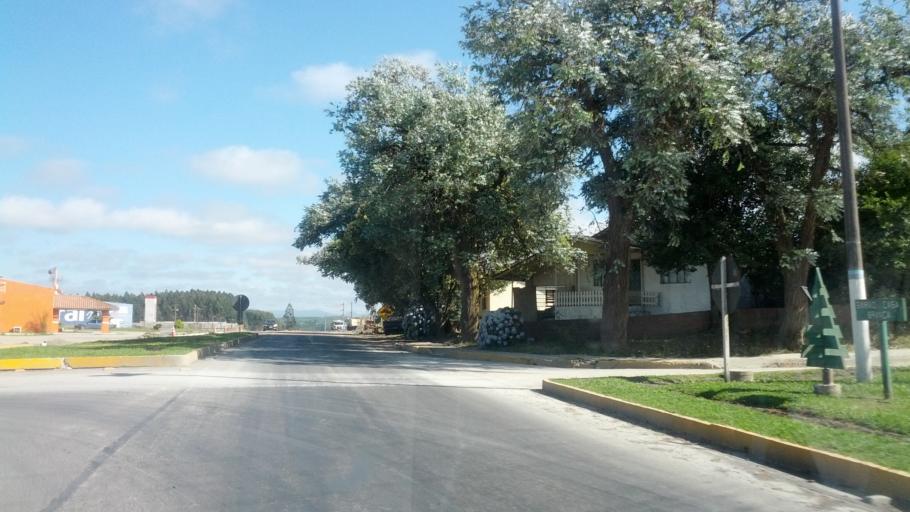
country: BR
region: Santa Catarina
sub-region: Otacilio Costa
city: Otacilio Costa
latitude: -27.4819
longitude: -50.1181
